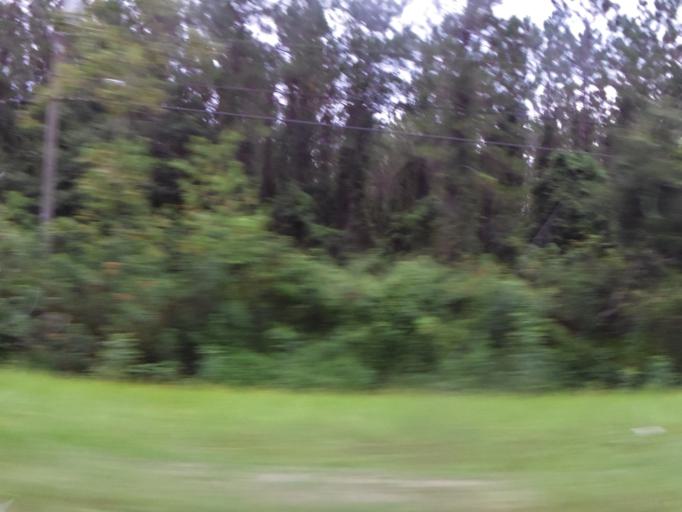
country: US
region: Florida
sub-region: Duval County
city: Baldwin
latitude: 30.3055
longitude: -82.0083
